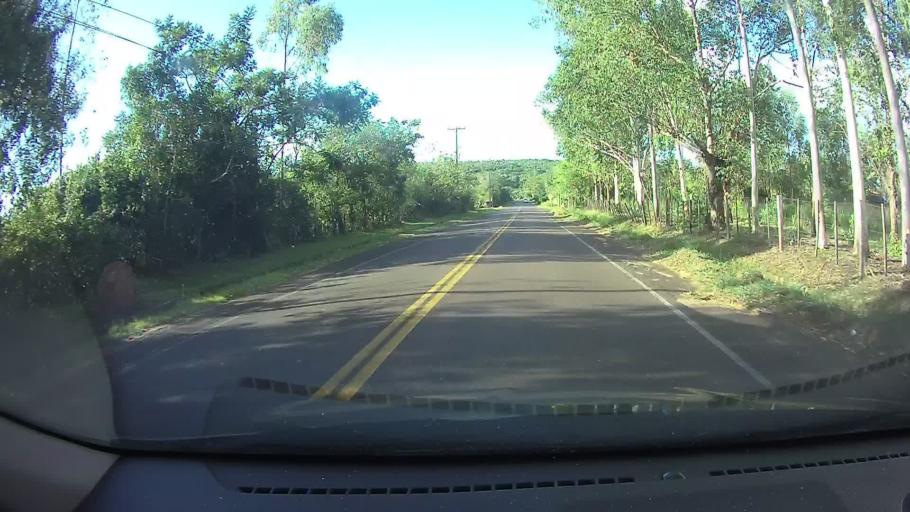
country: PY
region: Cordillera
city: Altos
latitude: -25.1922
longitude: -57.2242
